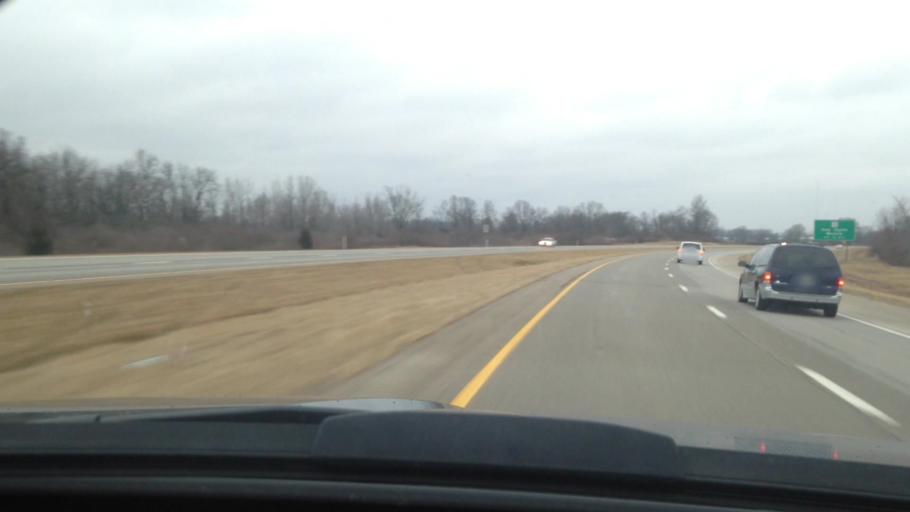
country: US
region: Indiana
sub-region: Delaware County
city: Muncie
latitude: 40.1566
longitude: -85.3535
